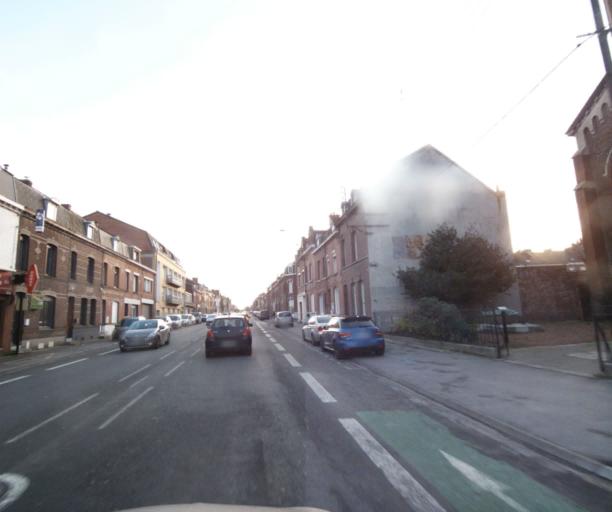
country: FR
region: Nord-Pas-de-Calais
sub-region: Departement du Nord
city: Anzin
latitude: 50.3631
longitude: 3.5083
